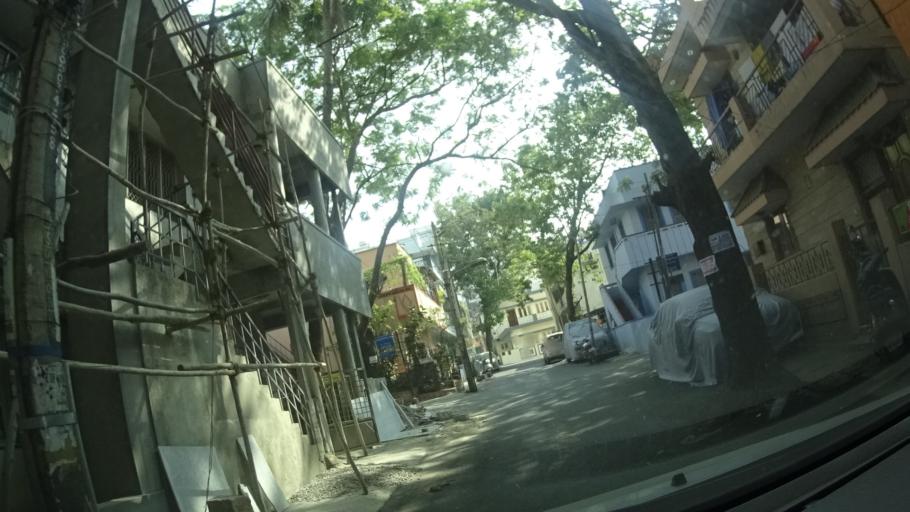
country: IN
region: Karnataka
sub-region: Bangalore Urban
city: Bangalore
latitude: 12.9428
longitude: 77.5608
